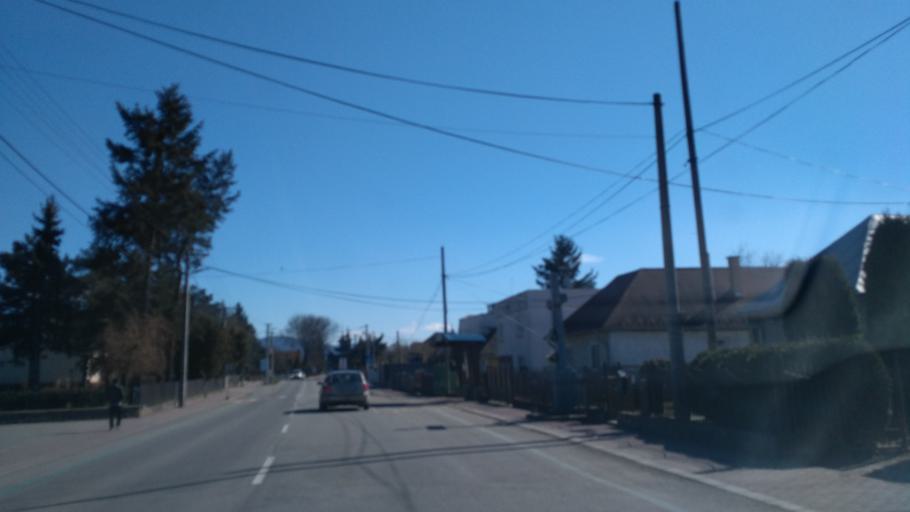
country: SK
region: Kosicky
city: Kosice
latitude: 48.6359
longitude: 21.2971
